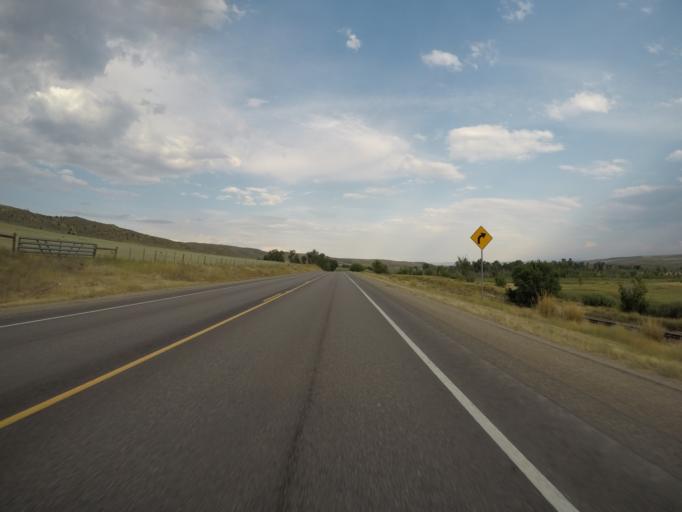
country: US
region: Colorado
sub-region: Moffat County
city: Craig
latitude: 40.5249
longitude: -107.4084
